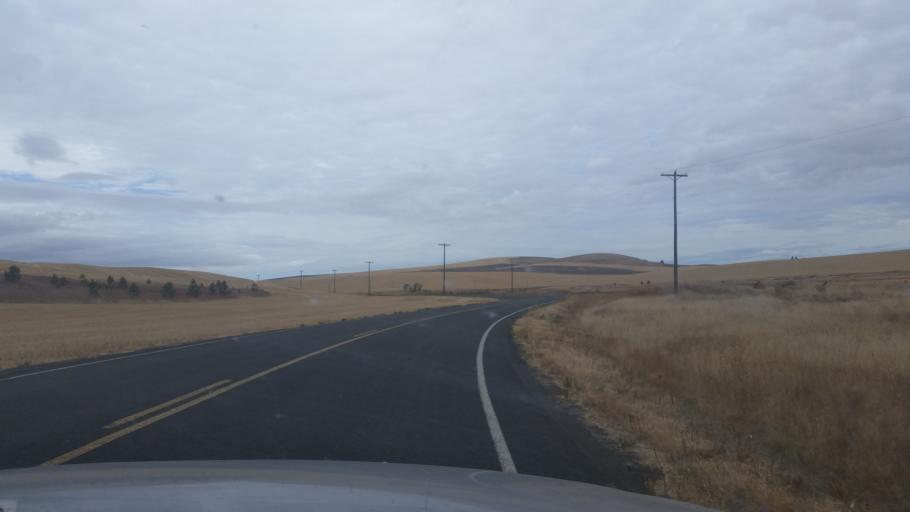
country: US
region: Washington
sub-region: Spokane County
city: Medical Lake
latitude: 47.5217
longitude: -117.9081
